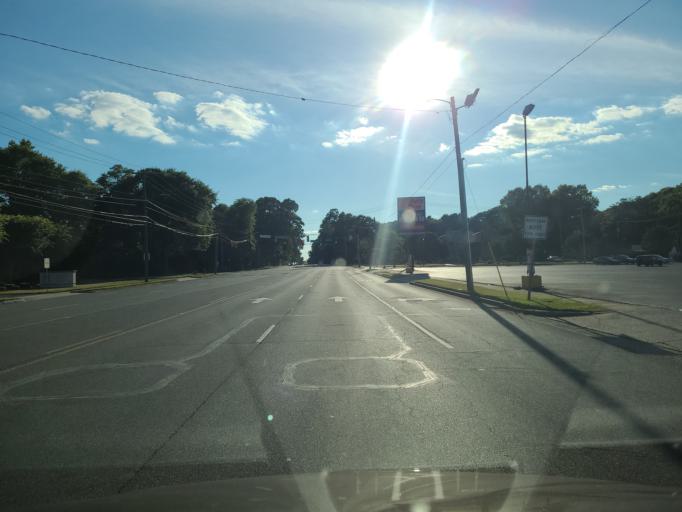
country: US
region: North Carolina
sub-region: Gaston County
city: Gastonia
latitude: 35.2624
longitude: -81.1571
